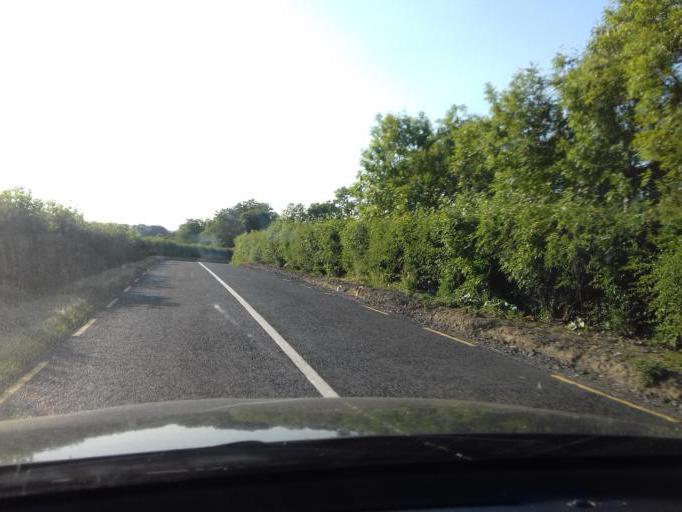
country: IE
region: Leinster
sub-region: An Mhi
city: Ashbourne
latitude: 53.4949
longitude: -6.3381
